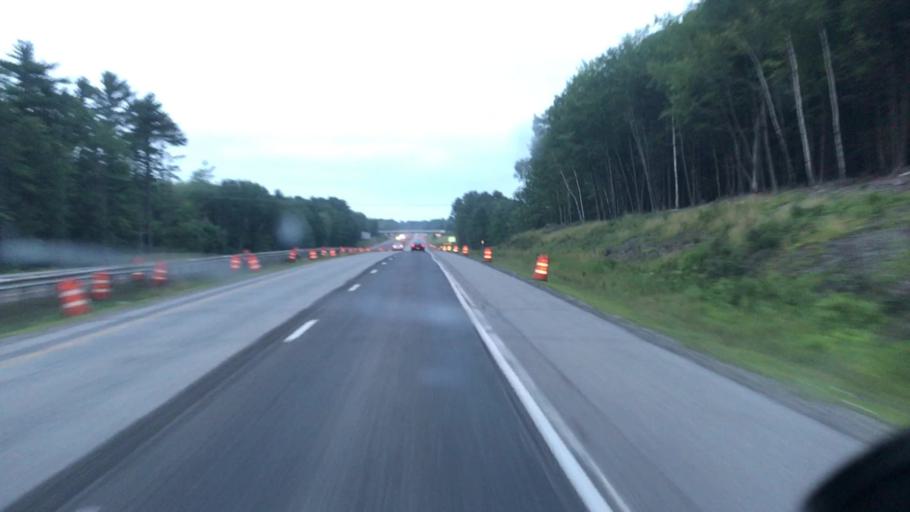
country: US
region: Maine
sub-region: Androscoggin County
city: Auburn
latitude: 44.0493
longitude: -70.2355
